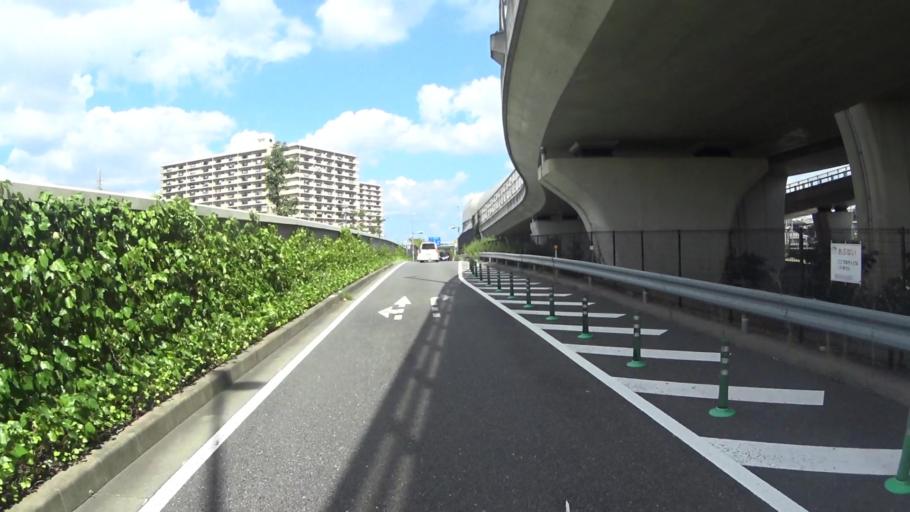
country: JP
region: Kyoto
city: Yawata
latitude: 34.8922
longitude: 135.7160
